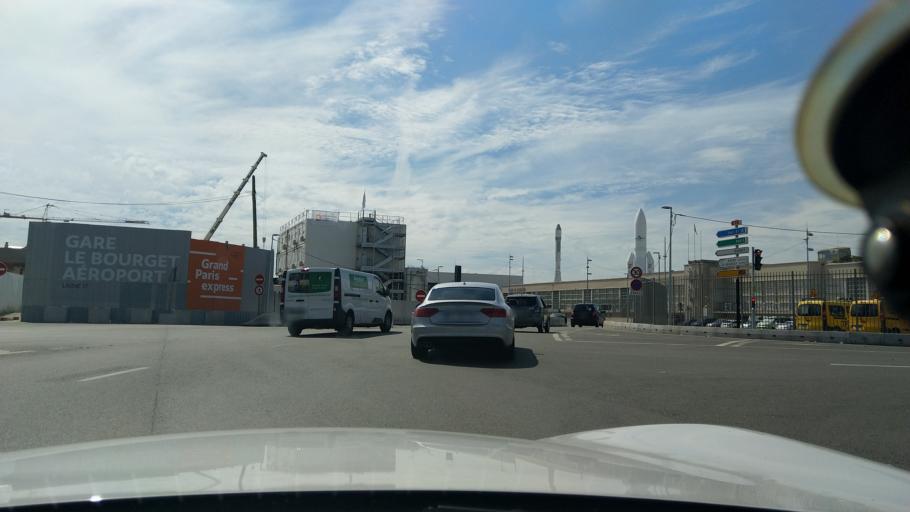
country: FR
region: Ile-de-France
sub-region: Departement de Seine-Saint-Denis
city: Le Bourget
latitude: 48.9487
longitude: 2.4382
